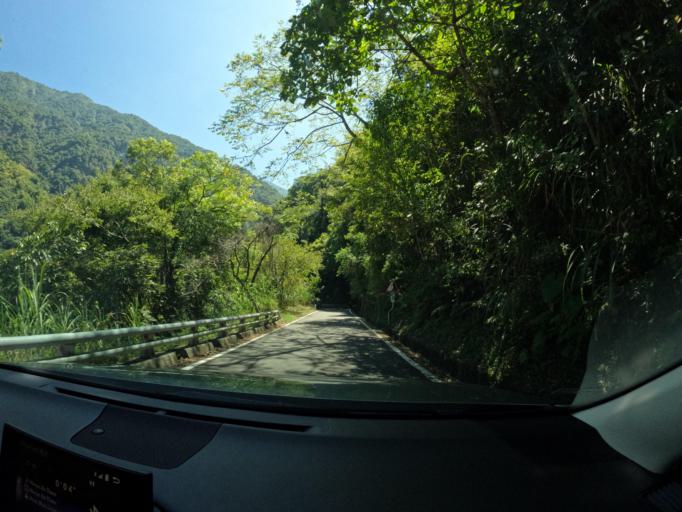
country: TW
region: Taiwan
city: Yujing
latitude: 23.2611
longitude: 120.8457
